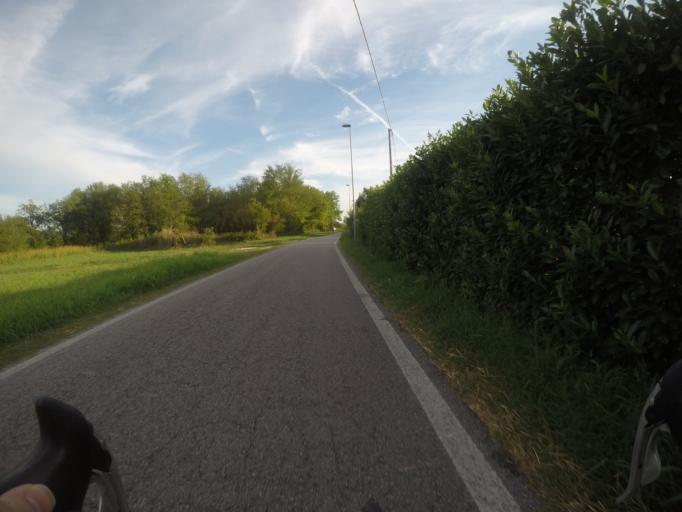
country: IT
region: Veneto
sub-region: Provincia di Rovigo
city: Pincara
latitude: 45.0018
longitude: 11.6098
